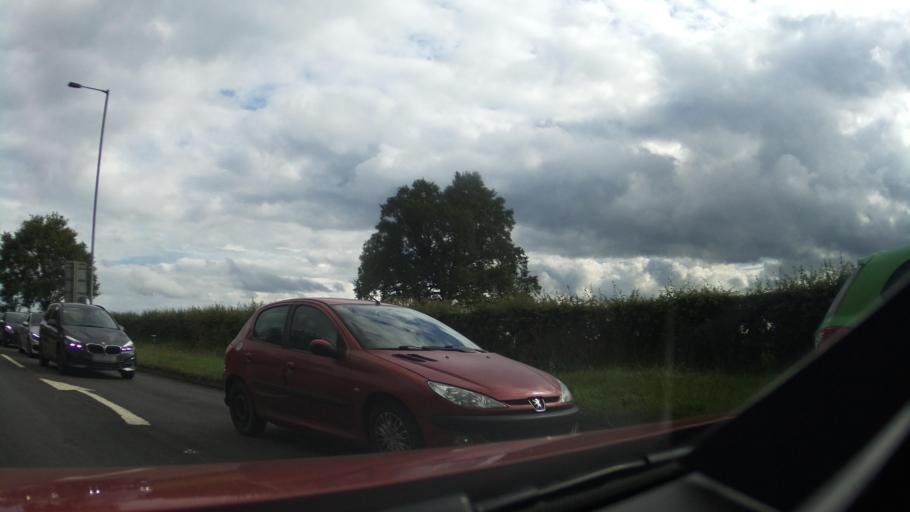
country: GB
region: England
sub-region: Dudley
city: Kingswinford
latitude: 52.5267
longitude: -2.1784
